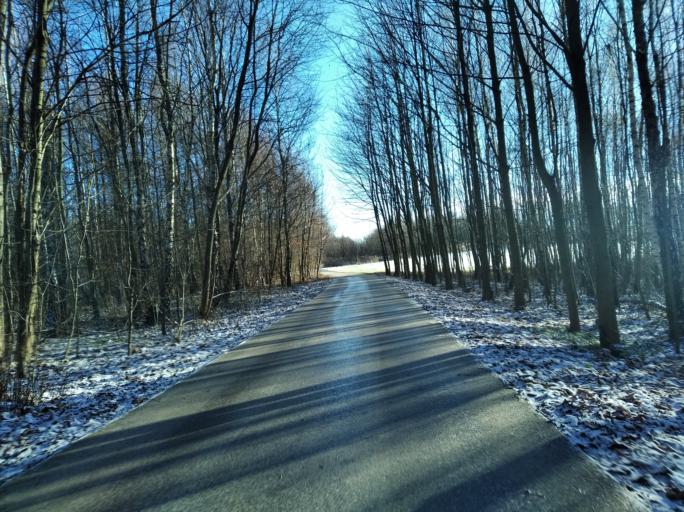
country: PL
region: Subcarpathian Voivodeship
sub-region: Powiat ropczycko-sedziszowski
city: Iwierzyce
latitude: 49.9588
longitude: 21.7533
